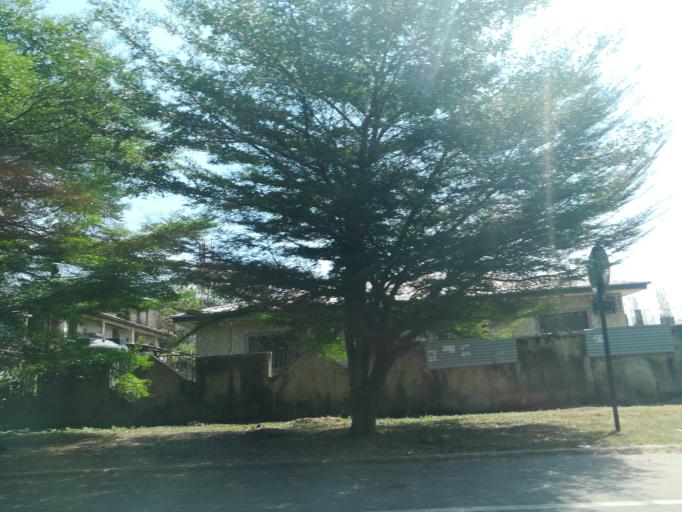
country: NG
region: Abuja Federal Capital Territory
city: Abuja
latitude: 9.0648
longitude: 7.4258
